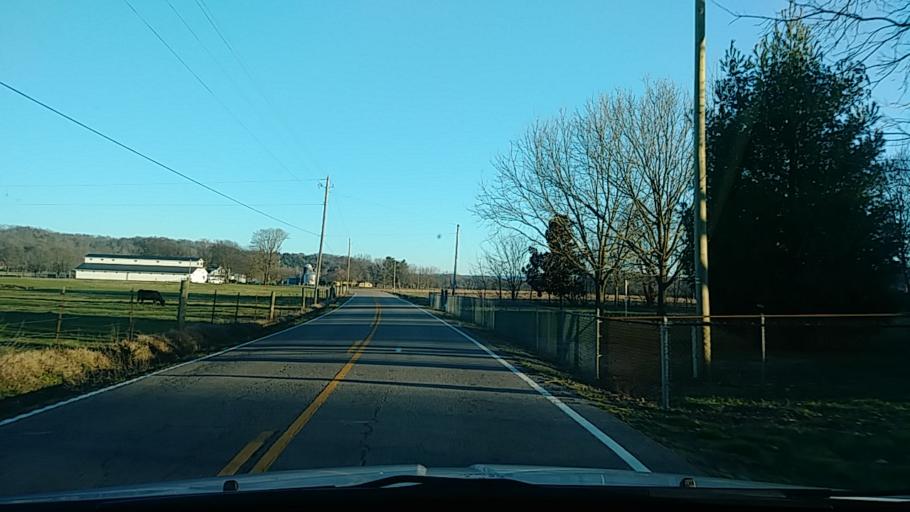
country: US
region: Tennessee
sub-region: Jefferson County
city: White Pine
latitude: 36.1388
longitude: -83.1394
